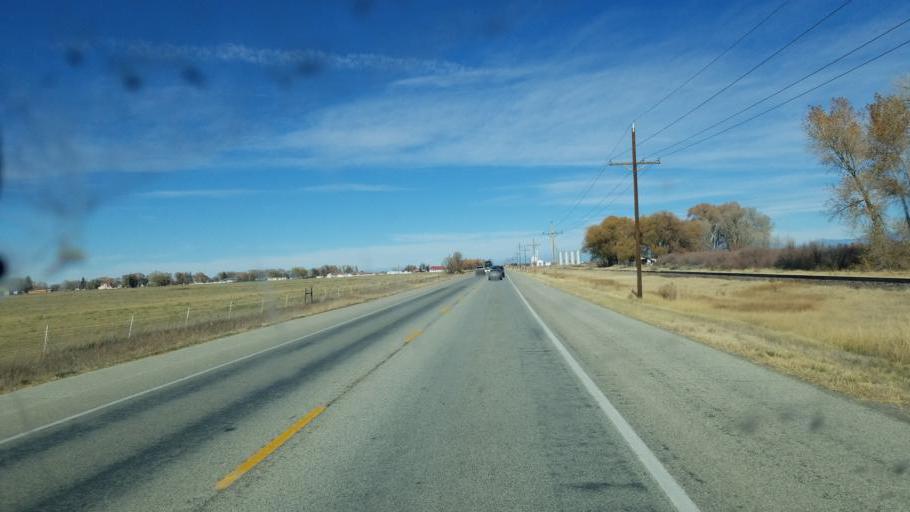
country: US
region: Colorado
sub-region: Conejos County
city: Conejos
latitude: 37.2187
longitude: -105.9760
